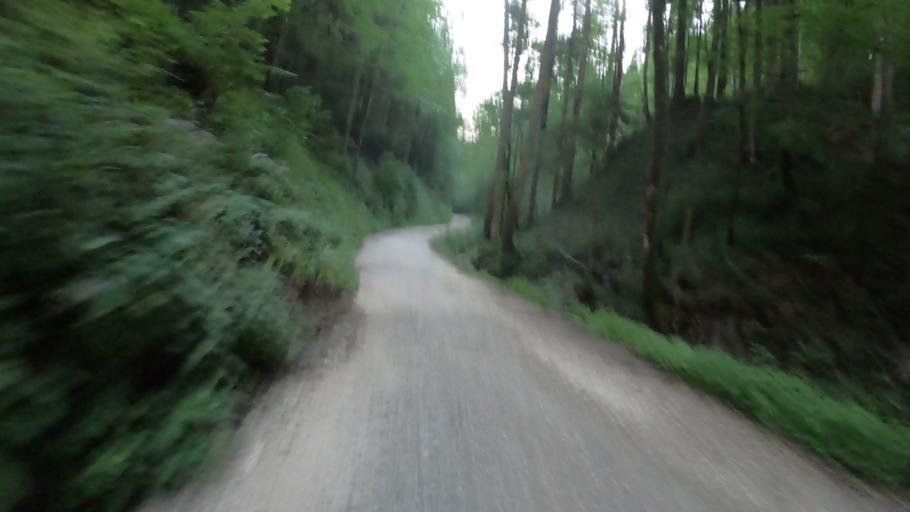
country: DE
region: Bavaria
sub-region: Upper Bavaria
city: Inzell
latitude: 47.7621
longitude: 12.7048
